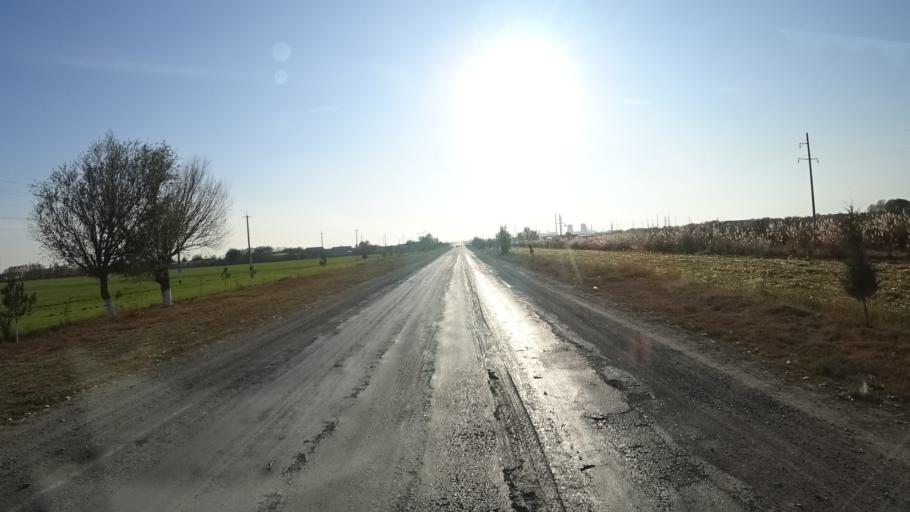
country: UZ
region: Navoiy
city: Beshrabot
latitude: 40.1783
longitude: 65.3476
